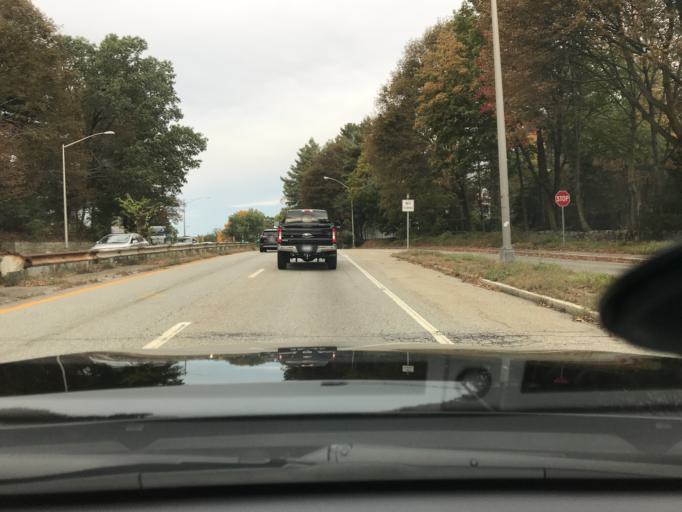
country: US
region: Massachusetts
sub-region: Norfolk County
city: Wellesley
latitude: 42.3146
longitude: -71.2653
